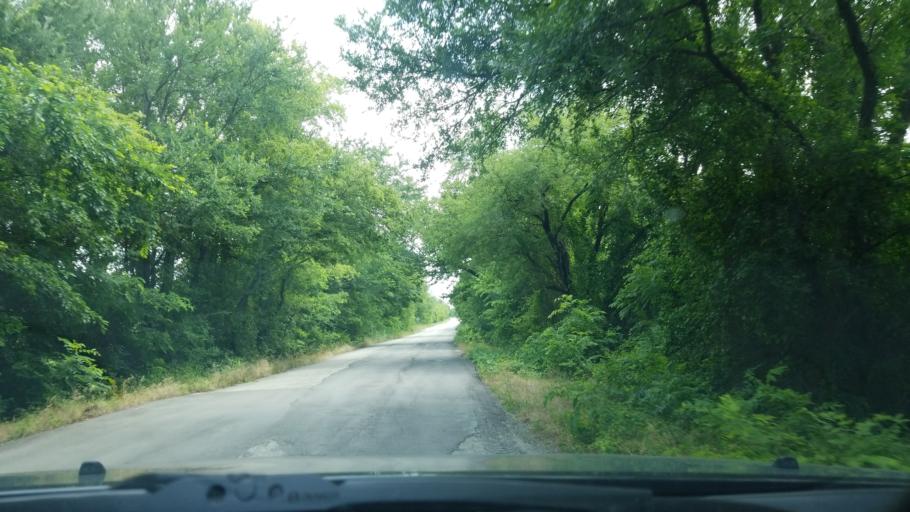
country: US
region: Texas
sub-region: Denton County
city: Sanger
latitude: 33.3141
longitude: -97.1743
